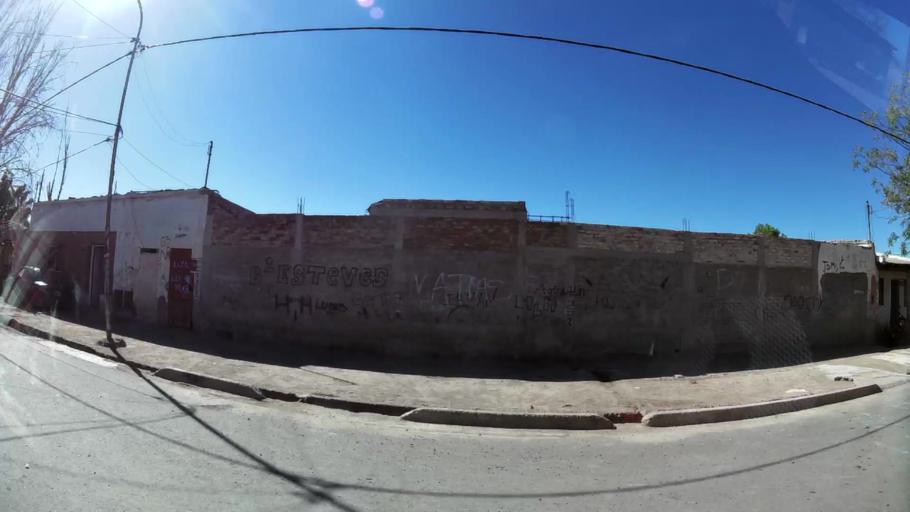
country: AR
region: Mendoza
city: Las Heras
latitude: -32.8374
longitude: -68.8147
